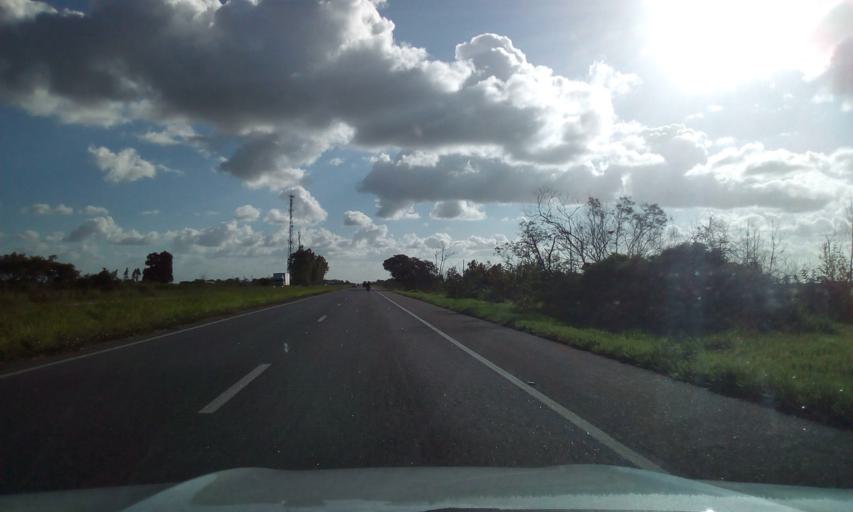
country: BR
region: Paraiba
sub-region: Cruz Do Espirito Santo
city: Cruz do Espirito Santo
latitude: -7.2025
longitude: -35.1083
